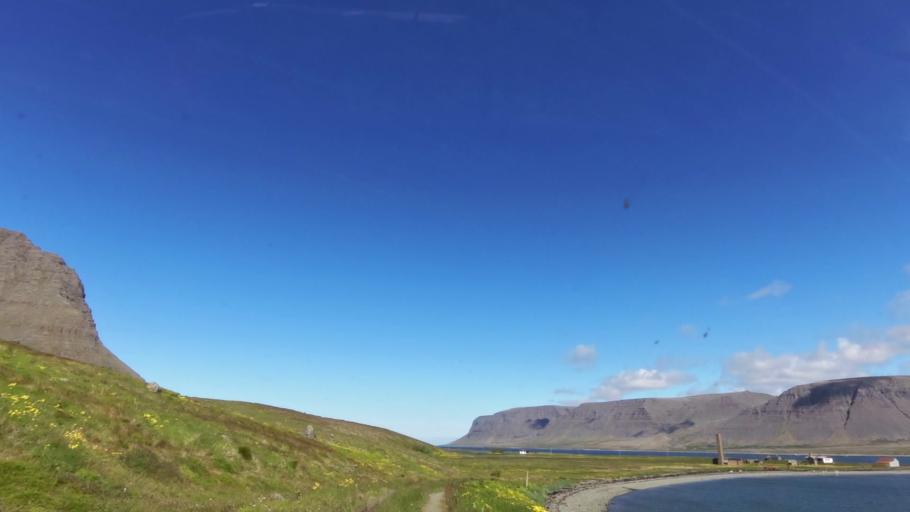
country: IS
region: West
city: Olafsvik
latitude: 65.6365
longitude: -23.9300
